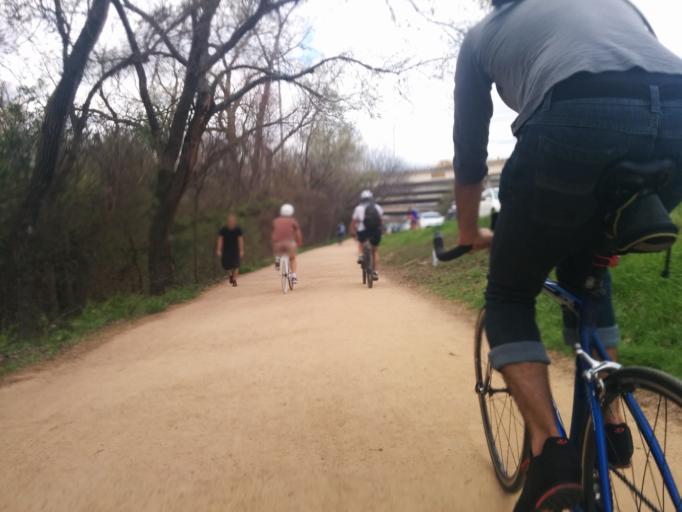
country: US
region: Texas
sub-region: Travis County
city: Rollingwood
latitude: 30.2740
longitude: -97.7695
